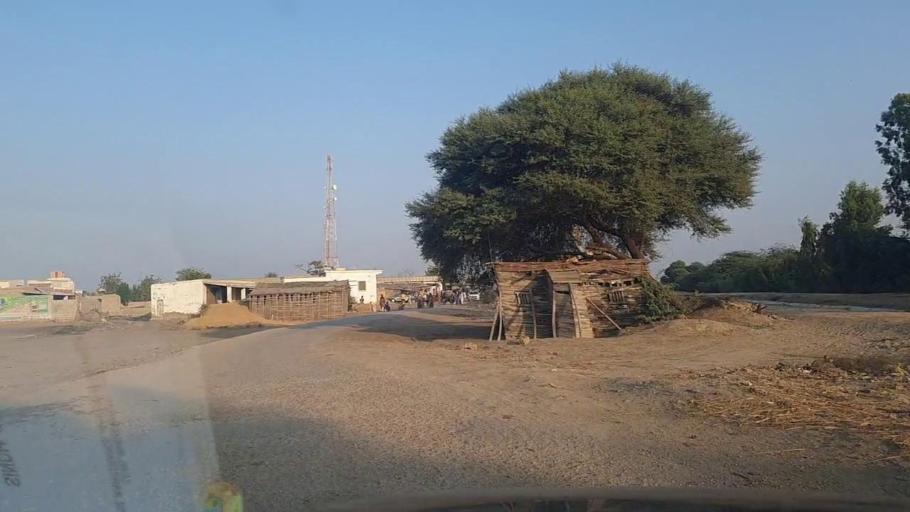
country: PK
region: Sindh
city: Keti Bandar
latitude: 24.3009
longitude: 67.6026
